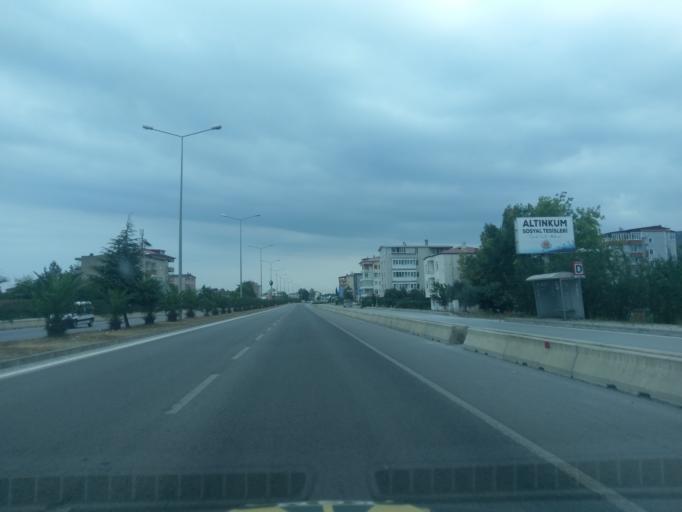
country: TR
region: Samsun
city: Taflan
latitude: 41.4023
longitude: 36.1883
